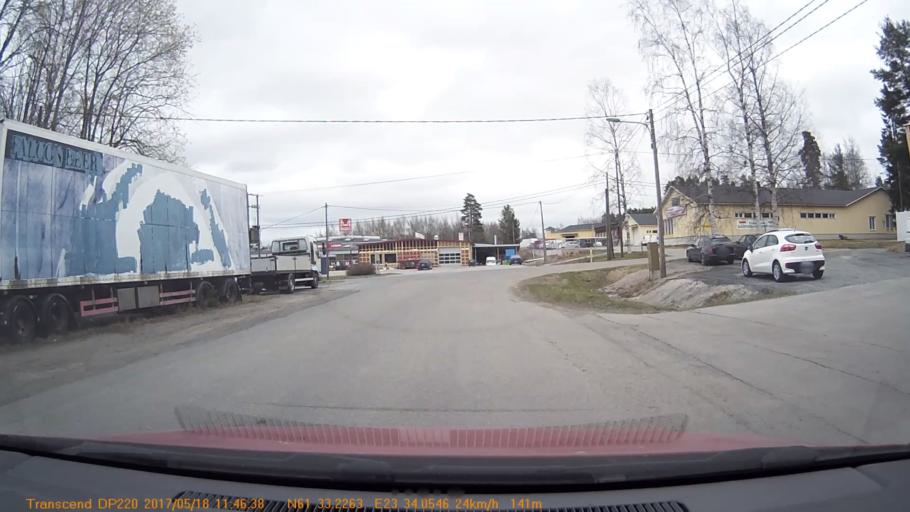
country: FI
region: Pirkanmaa
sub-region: Tampere
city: Yloejaervi
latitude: 61.5538
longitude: 23.5674
